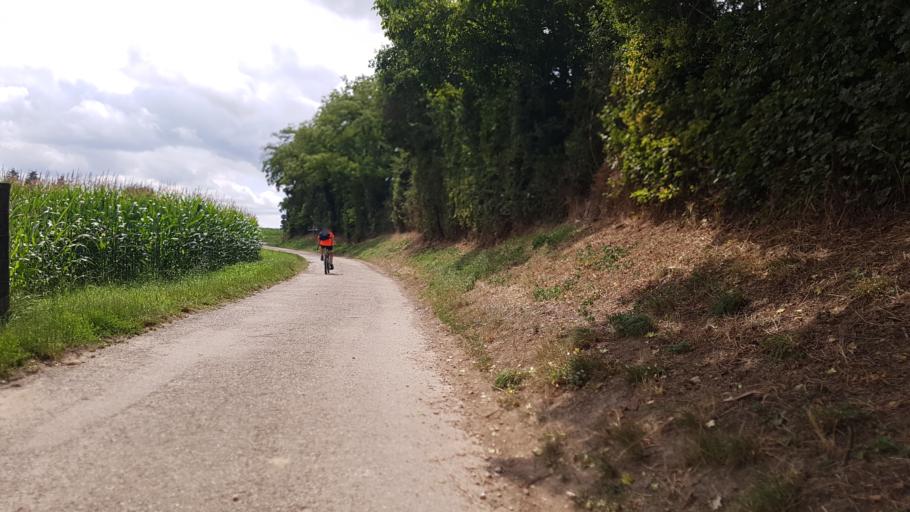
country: FR
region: Rhone-Alpes
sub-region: Departement du Rhone
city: Genas
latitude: 45.7375
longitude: 4.9928
